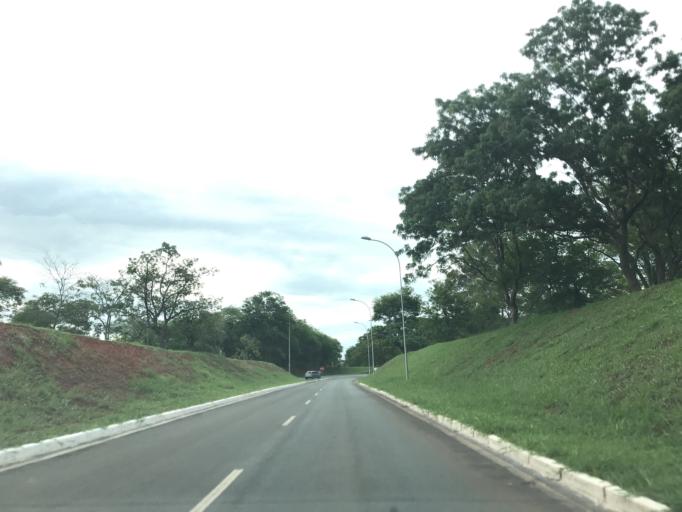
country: BR
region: Federal District
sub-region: Brasilia
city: Brasilia
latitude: -15.8342
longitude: -47.8997
